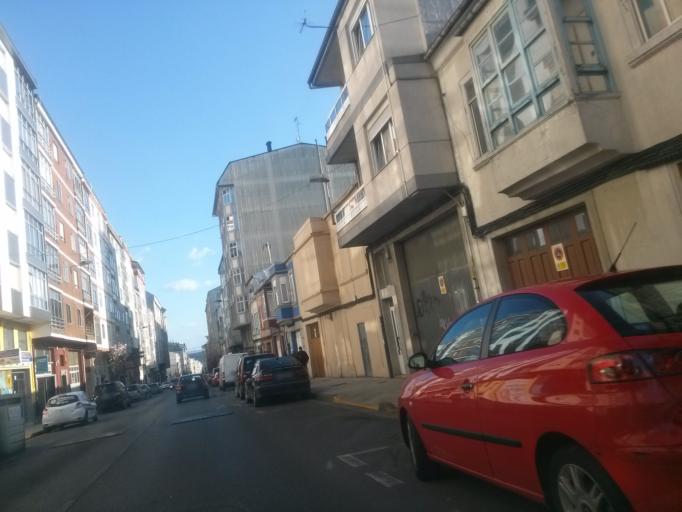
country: ES
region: Galicia
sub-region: Provincia de Lugo
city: Lugo
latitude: 43.0179
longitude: -7.5672
